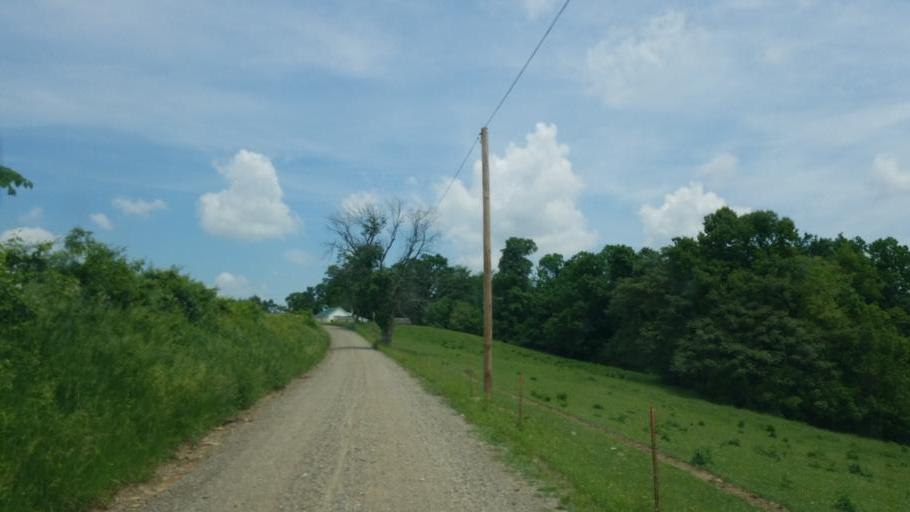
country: US
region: Ohio
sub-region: Tuscarawas County
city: Sugarcreek
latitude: 40.4287
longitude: -81.7459
